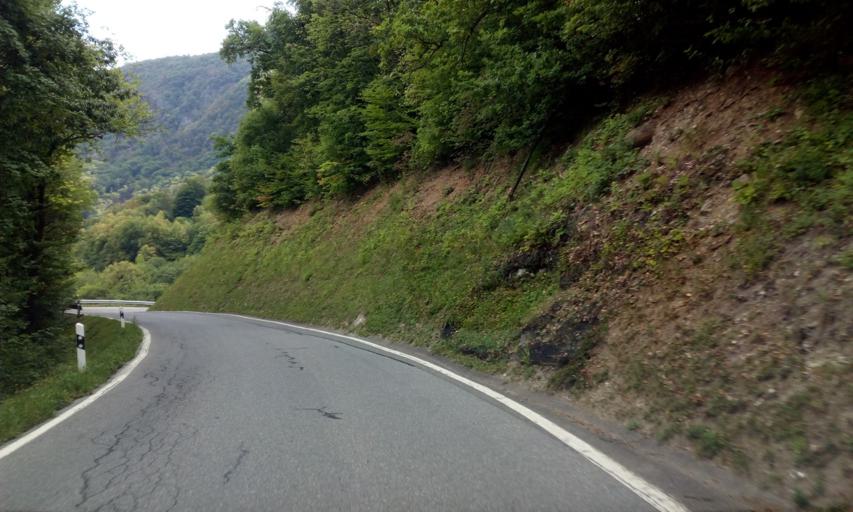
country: CH
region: Valais
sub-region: Monthey District
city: Vionnaz
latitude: 46.3122
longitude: 6.8941
